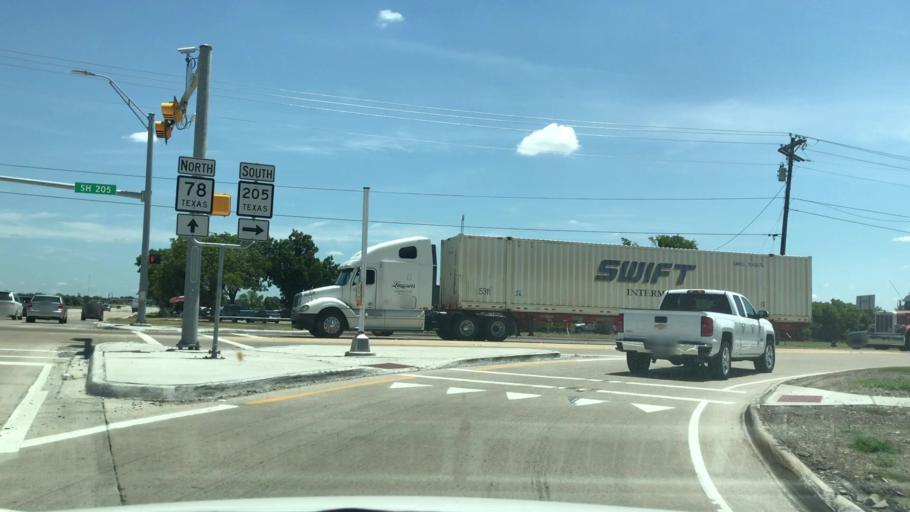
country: US
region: Texas
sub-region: Collin County
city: Lavon
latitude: 33.0223
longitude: -96.4566
